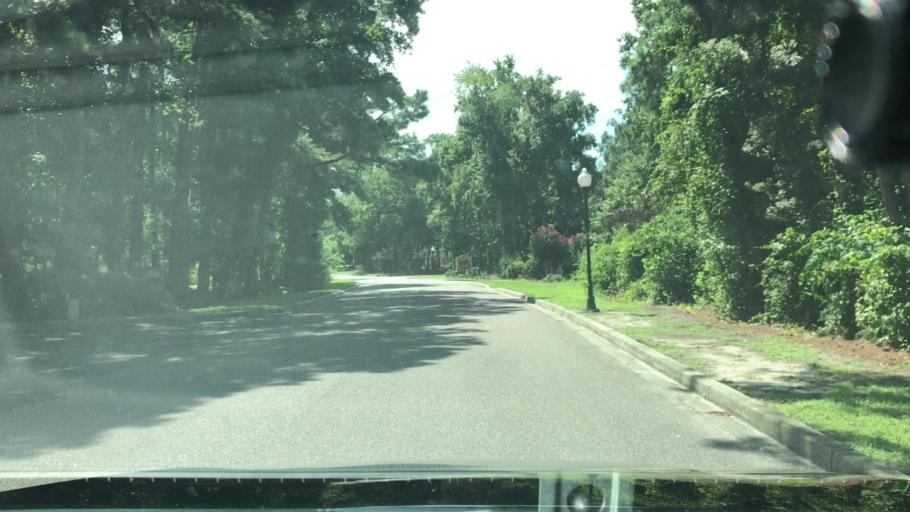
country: US
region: South Carolina
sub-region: Beaufort County
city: Hilton Head Island
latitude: 32.2150
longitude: -80.7298
